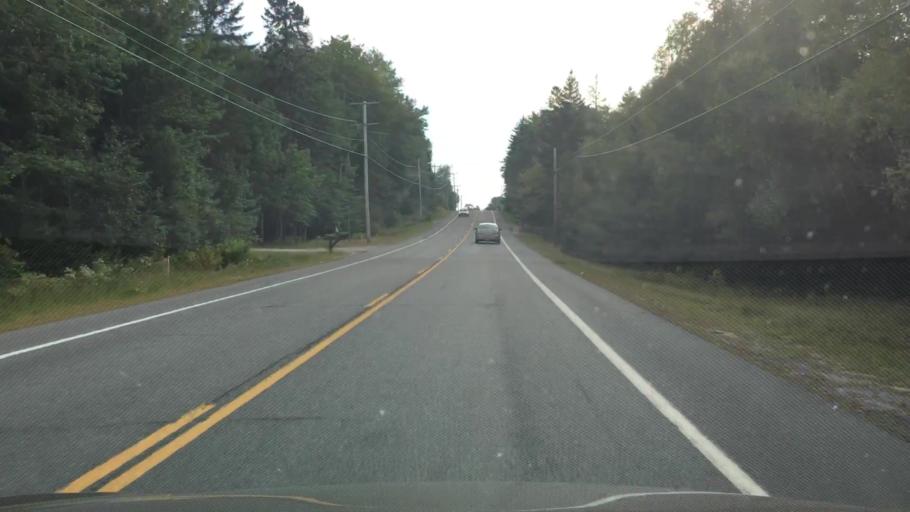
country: US
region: Maine
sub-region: Hancock County
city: Surry
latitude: 44.4571
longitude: -68.5471
